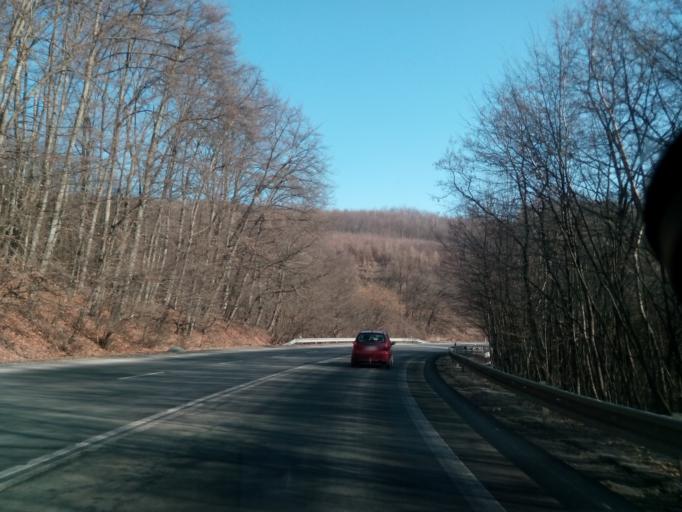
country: SK
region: Kosicky
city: Secovce
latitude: 48.7361
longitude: 21.5386
